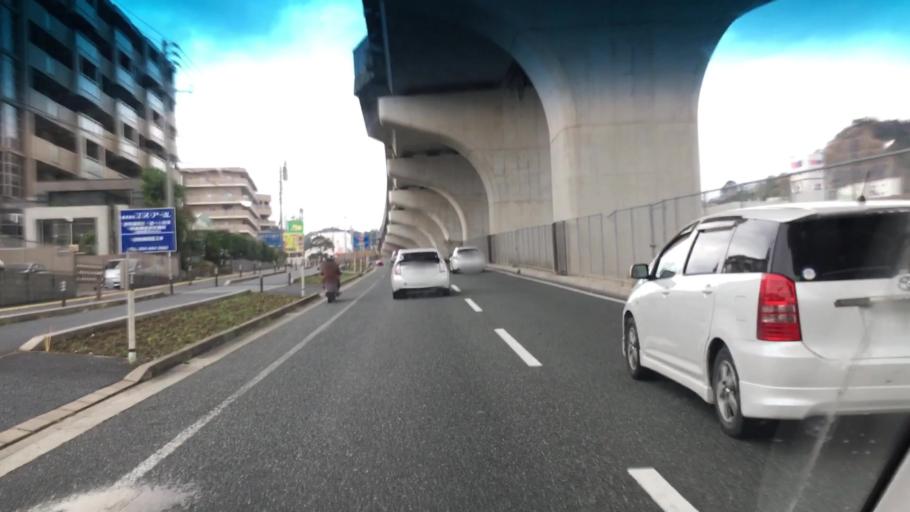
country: JP
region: Fukuoka
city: Maebaru-chuo
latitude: 33.5692
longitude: 130.2994
